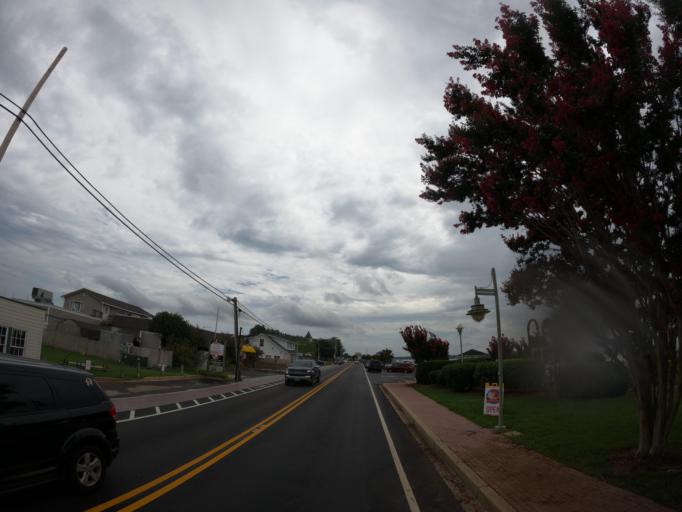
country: US
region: Maryland
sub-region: Calvert County
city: Solomons
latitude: 38.3241
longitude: -76.4612
